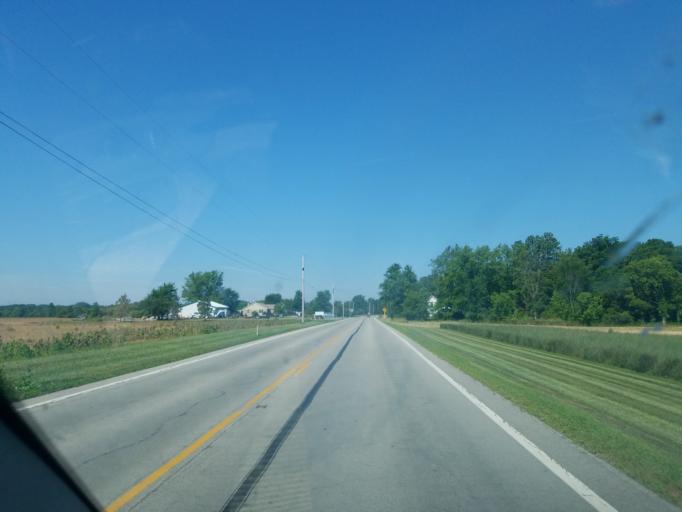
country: US
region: Ohio
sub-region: Logan County
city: Russells Point
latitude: 40.4640
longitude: -83.8240
